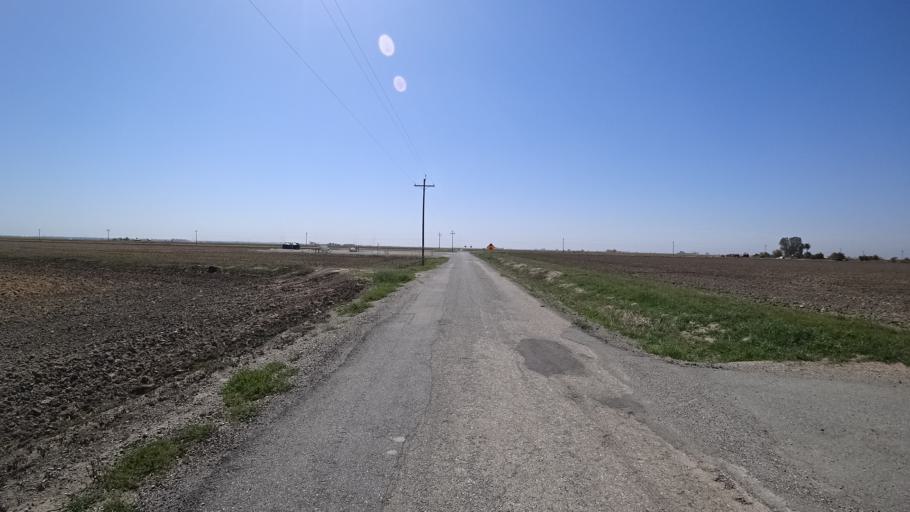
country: US
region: California
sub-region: Glenn County
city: Willows
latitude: 39.5233
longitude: -122.0746
